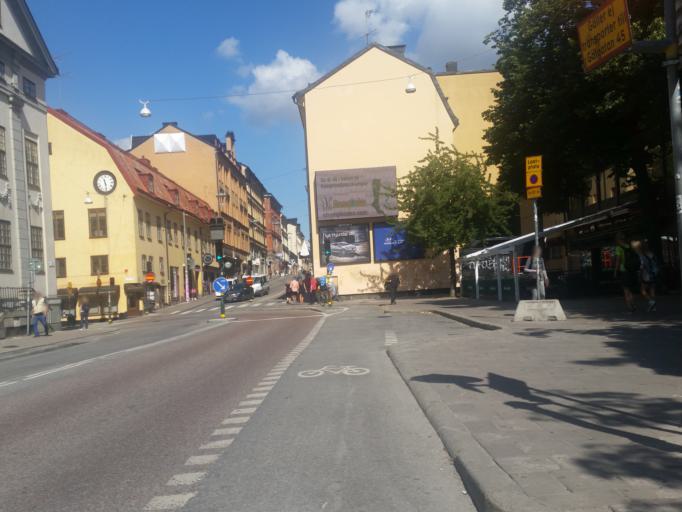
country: SE
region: Stockholm
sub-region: Stockholms Kommun
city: Stockholm
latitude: 59.3153
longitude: 18.0729
